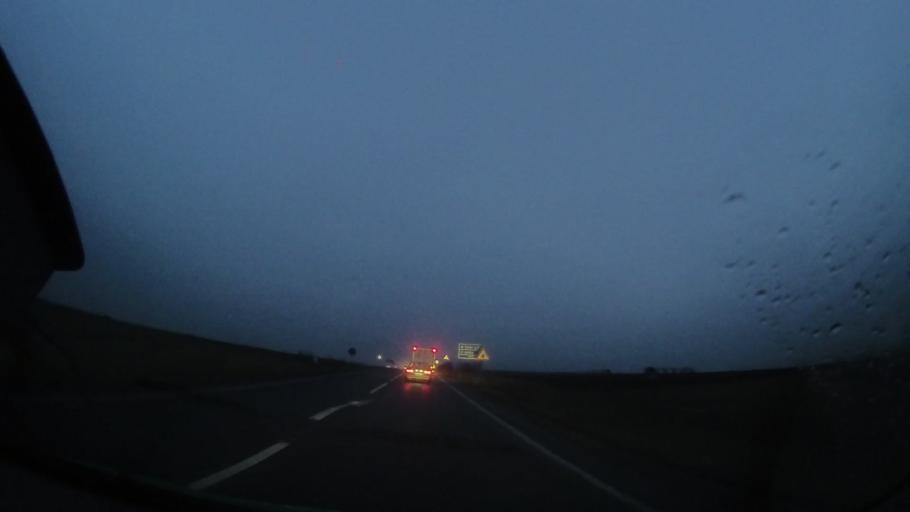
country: RO
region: Harghita
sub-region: Comuna Ditrau
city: Ditrau
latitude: 46.8301
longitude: 25.4923
